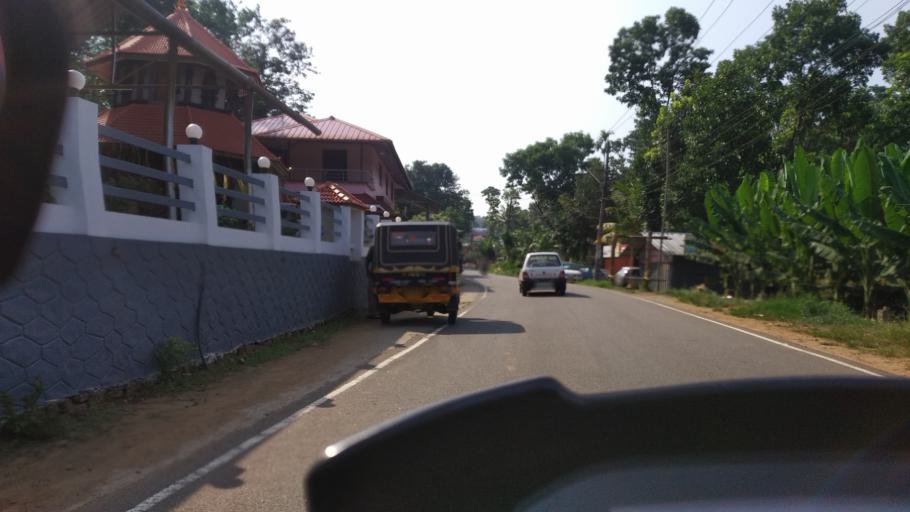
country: IN
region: Kerala
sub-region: Kottayam
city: Palackattumala
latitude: 9.8107
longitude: 76.5710
